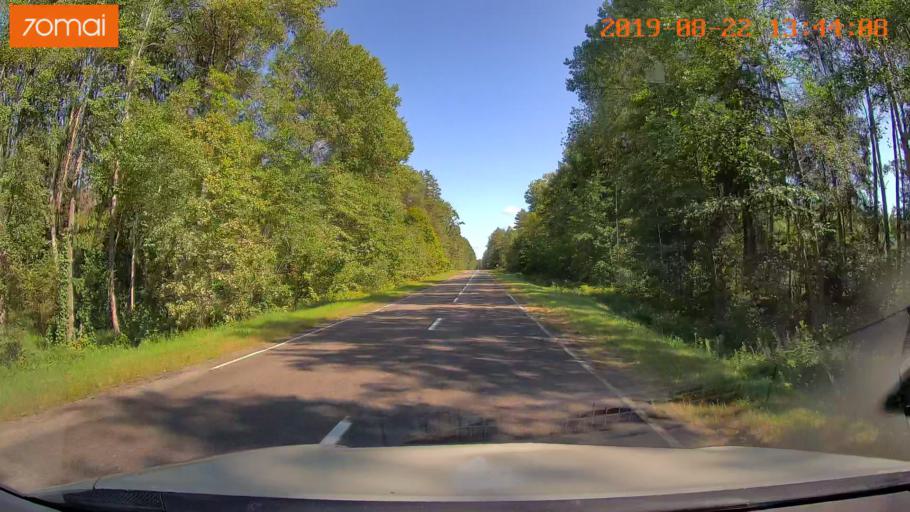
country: BY
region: Mogilev
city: Asipovichy
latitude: 53.2438
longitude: 28.4534
